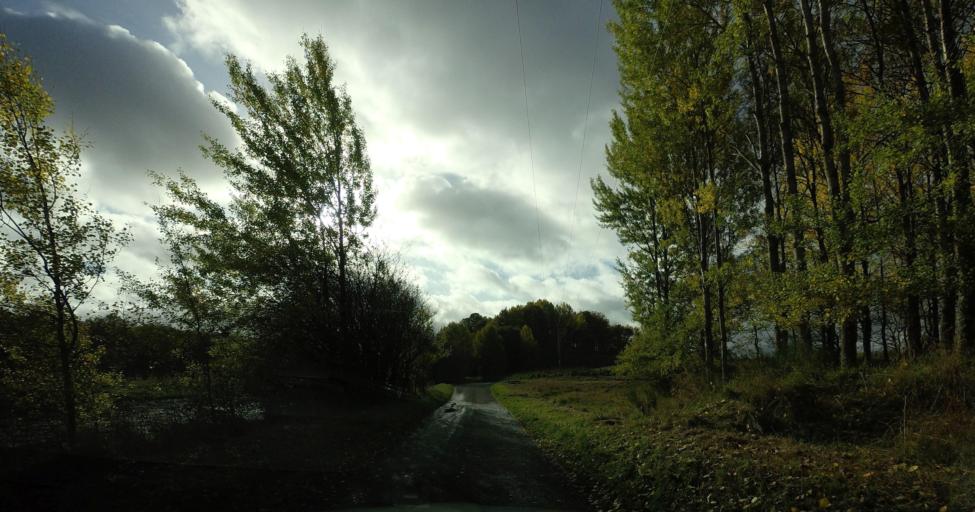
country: GB
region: Scotland
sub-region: Highland
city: Grantown on Spey
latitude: 57.3171
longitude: -3.6160
